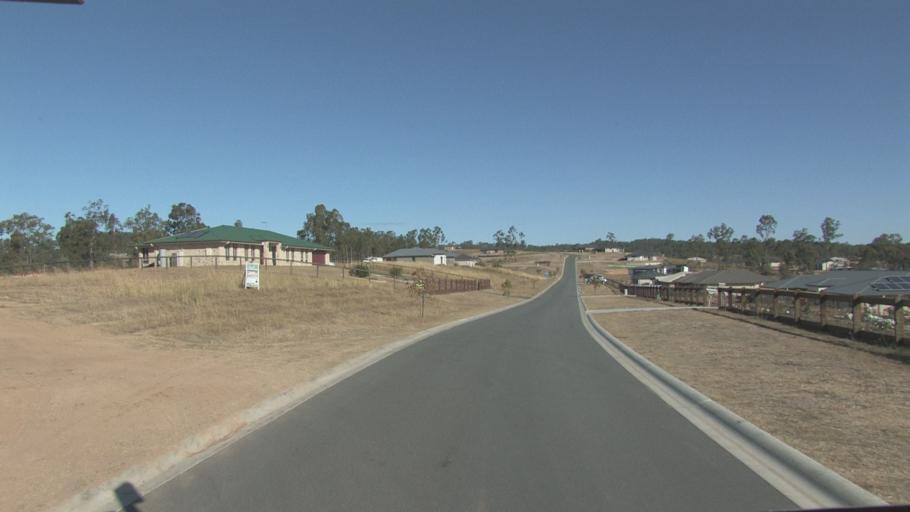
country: AU
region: Queensland
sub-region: Logan
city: Cedar Vale
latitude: -27.8683
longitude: 153.0530
